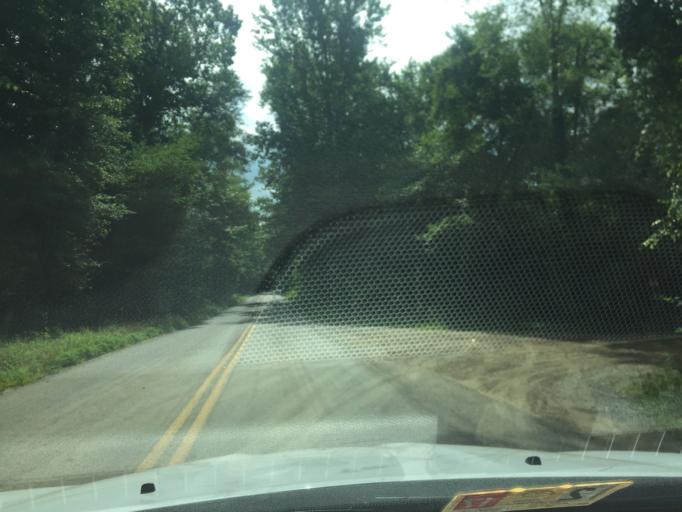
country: US
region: Virginia
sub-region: Charles City County
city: Charles City
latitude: 37.4109
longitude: -77.0343
